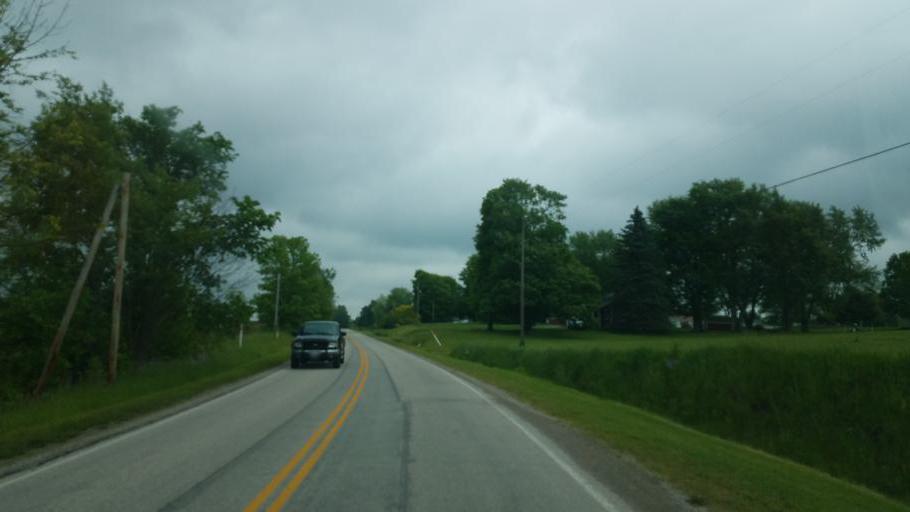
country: US
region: Ohio
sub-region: Ashland County
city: Ashland
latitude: 40.7732
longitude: -82.3545
